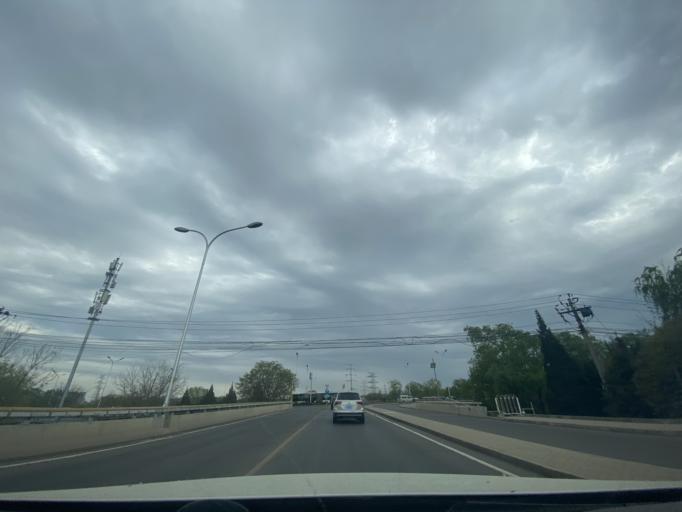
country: CN
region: Beijing
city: Haidian
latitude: 39.9751
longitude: 116.2789
